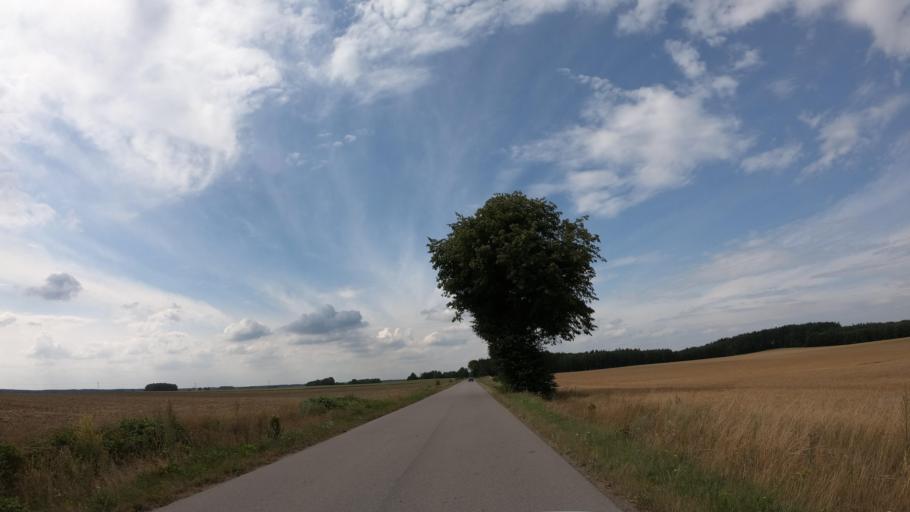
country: PL
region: West Pomeranian Voivodeship
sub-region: Powiat walecki
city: Tuczno
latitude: 53.2377
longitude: 16.1525
